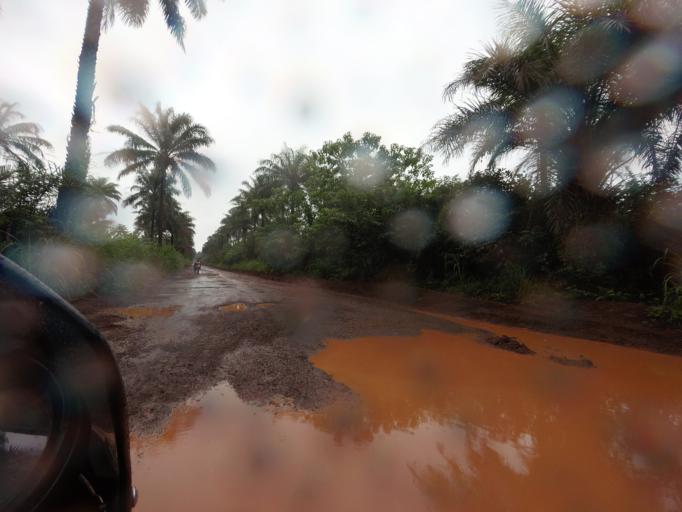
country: SL
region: Northern Province
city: Kambia
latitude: 9.1798
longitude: -12.8777
